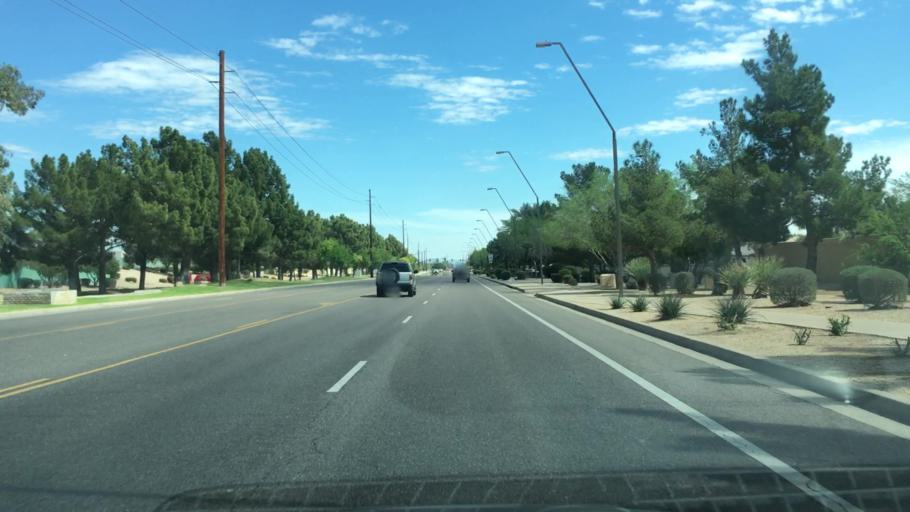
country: US
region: Arizona
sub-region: Maricopa County
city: Gilbert
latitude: 33.3642
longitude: -111.8162
